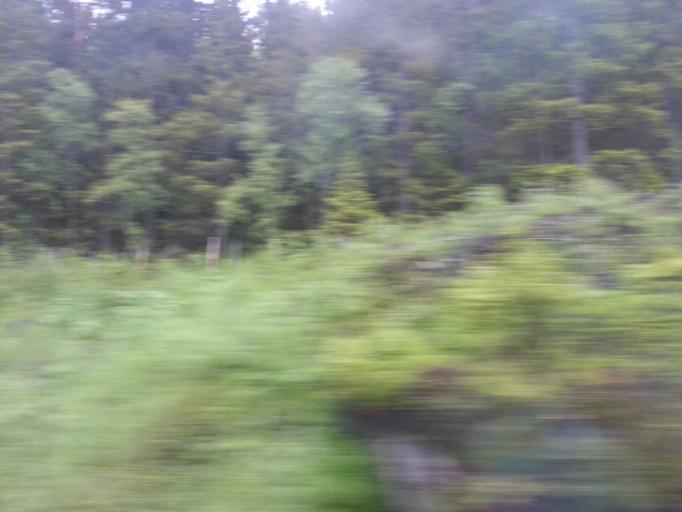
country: NO
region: Sor-Trondelag
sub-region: Rennebu
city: Berkak
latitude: 62.7761
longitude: 9.9898
